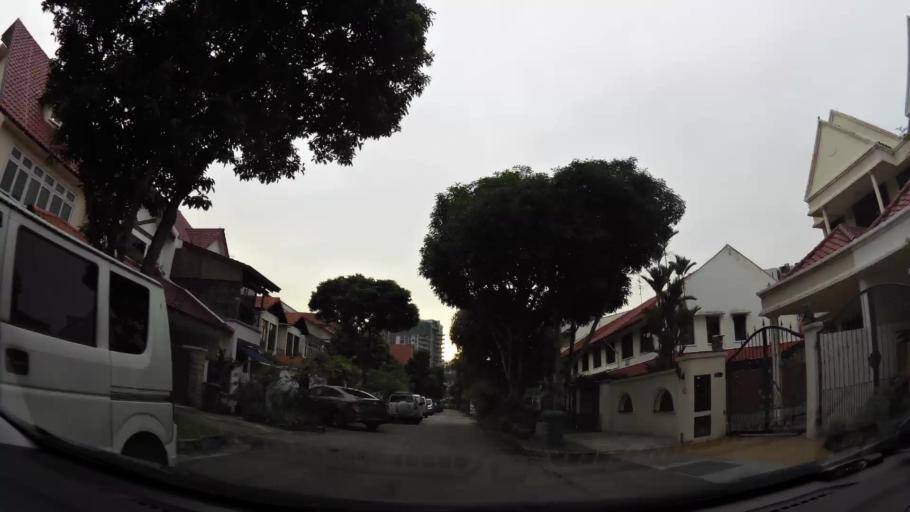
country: SG
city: Singapore
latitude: 1.3320
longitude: 103.8721
